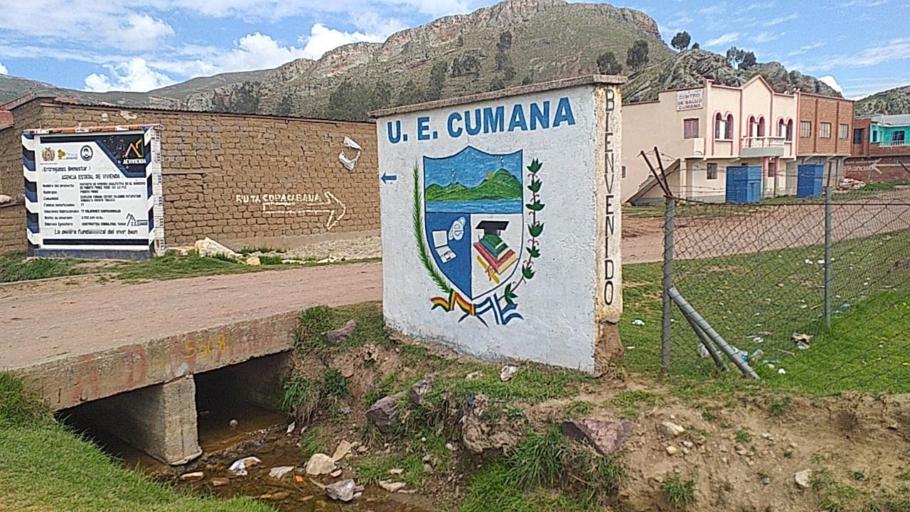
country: BO
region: La Paz
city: Batallas
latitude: -16.3490
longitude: -68.6347
